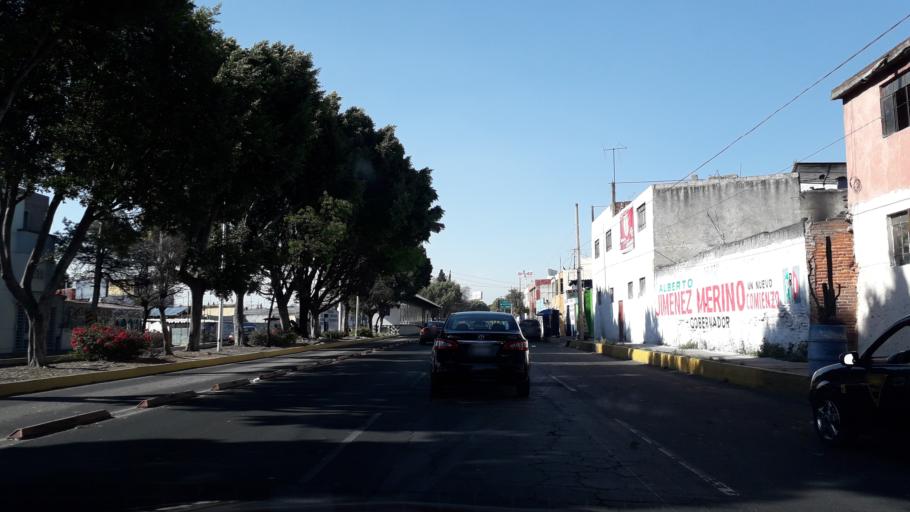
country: MX
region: Puebla
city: Puebla
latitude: 19.0592
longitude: -98.1924
